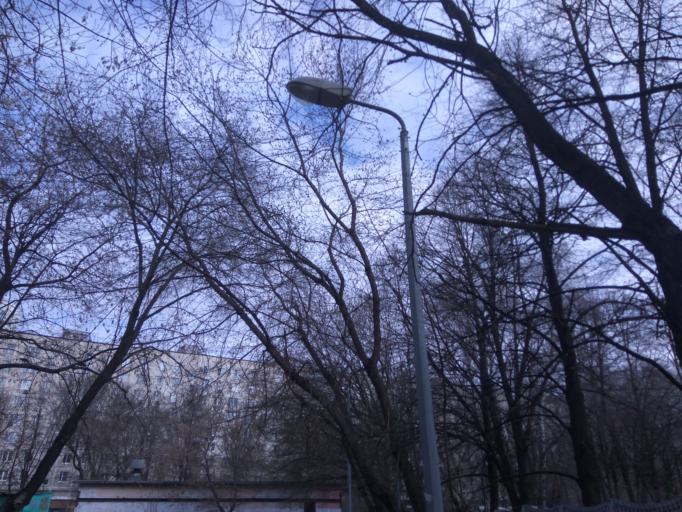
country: RU
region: Moskovskaya
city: Kozhukhovo
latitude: 55.6835
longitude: 37.6685
